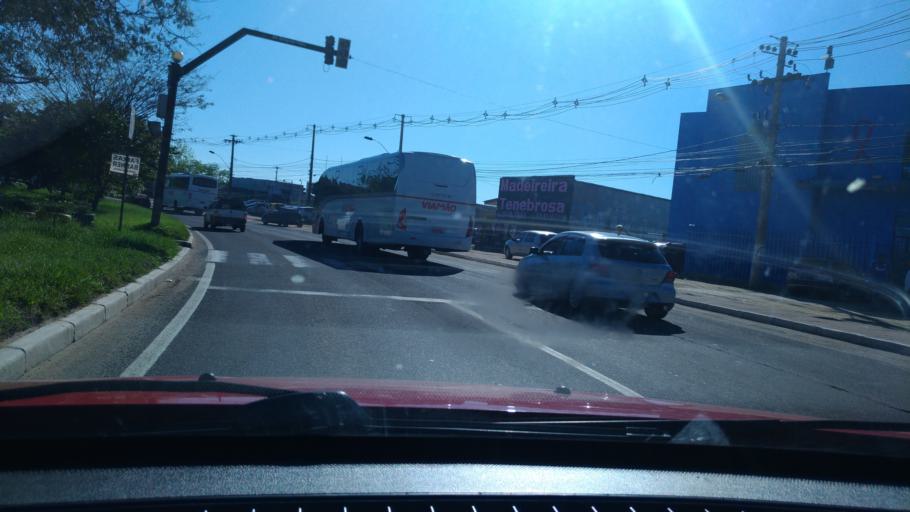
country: BR
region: Rio Grande do Sul
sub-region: Viamao
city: Viamao
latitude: -30.0923
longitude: -51.0641
